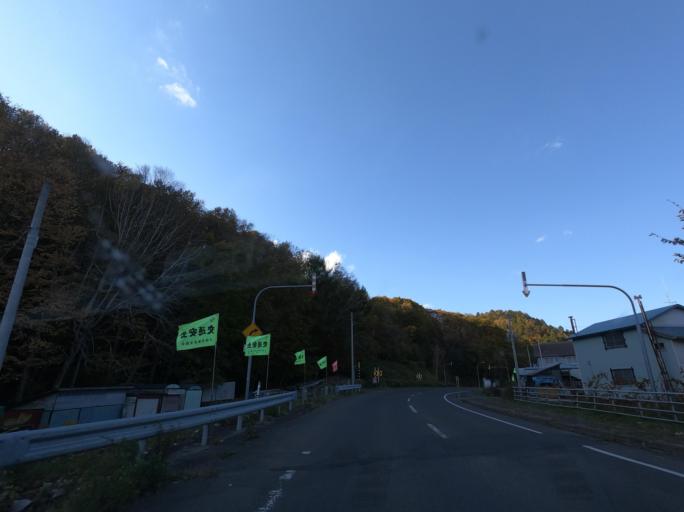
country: JP
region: Hokkaido
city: Iwamizawa
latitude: 42.9997
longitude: 142.0049
